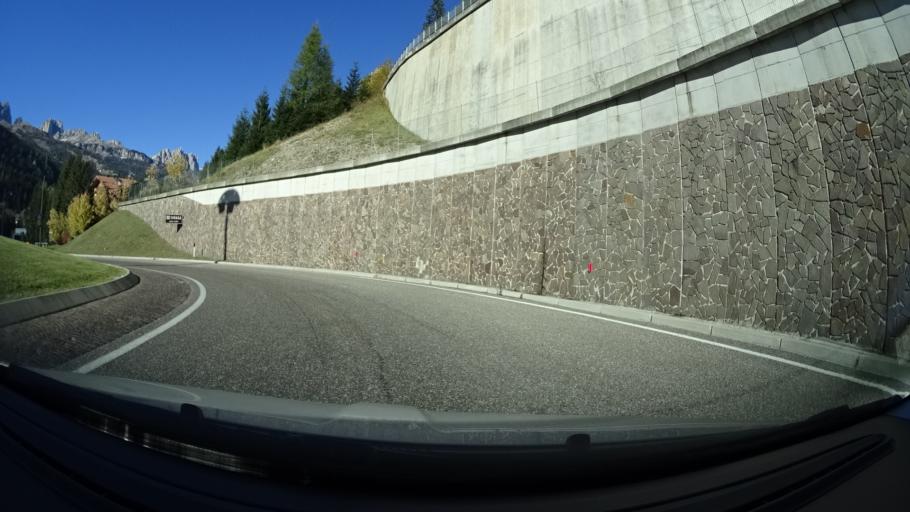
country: IT
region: Trentino-Alto Adige
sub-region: Provincia di Trento
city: Soraga
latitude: 46.3854
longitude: 11.6689
